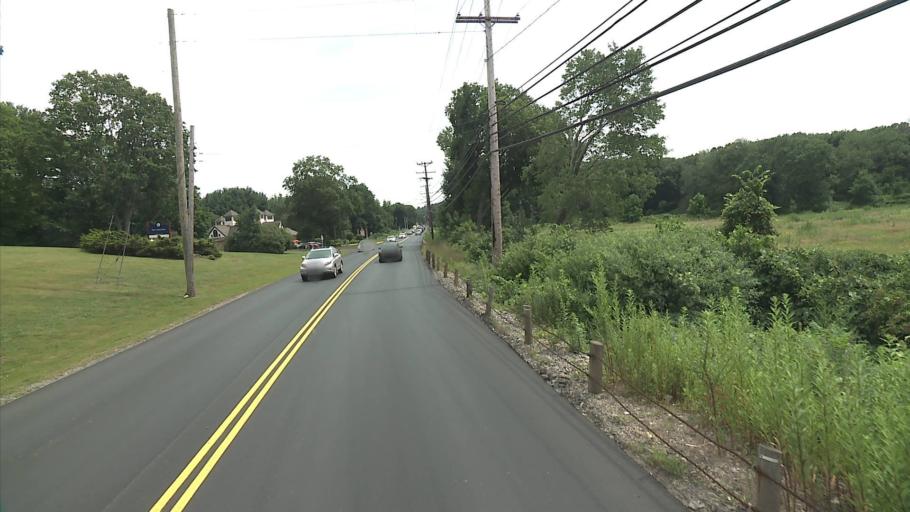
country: US
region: Connecticut
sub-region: New Haven County
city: Seymour
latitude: 41.4072
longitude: -73.0939
